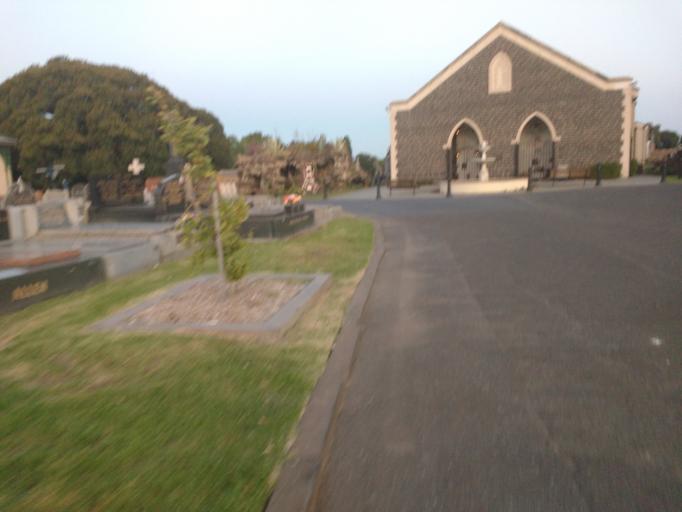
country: AU
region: Victoria
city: Carlton North
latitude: -37.7894
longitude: 144.9635
